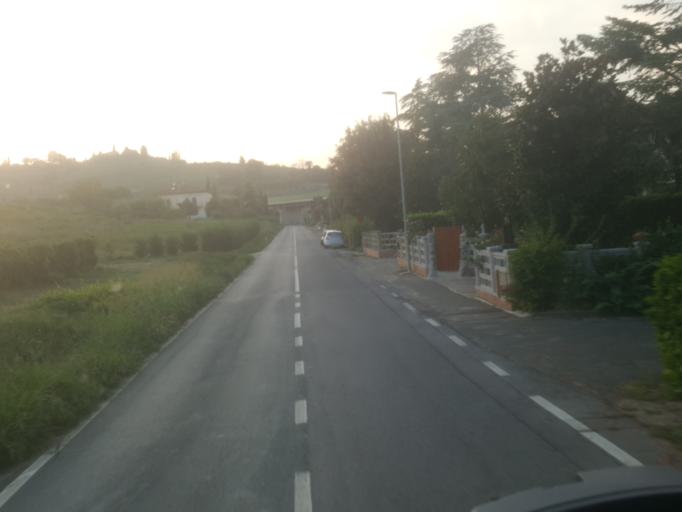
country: IT
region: Tuscany
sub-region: Province of Florence
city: Certaldo
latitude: 43.5311
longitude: 11.0367
